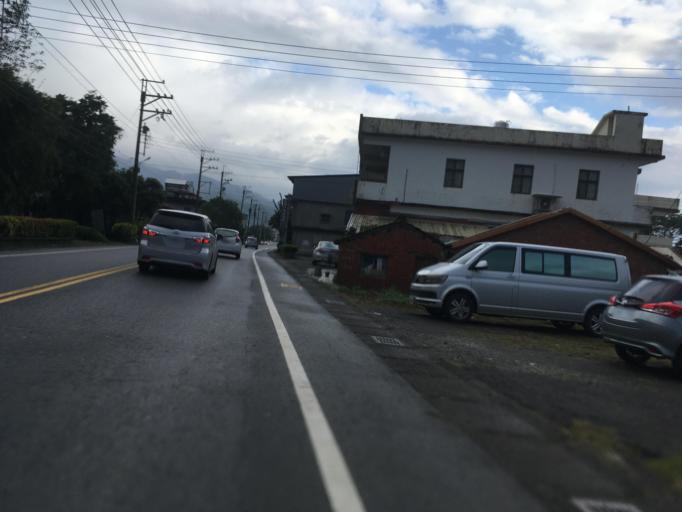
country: TW
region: Taiwan
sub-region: Yilan
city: Yilan
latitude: 24.8369
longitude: 121.8046
